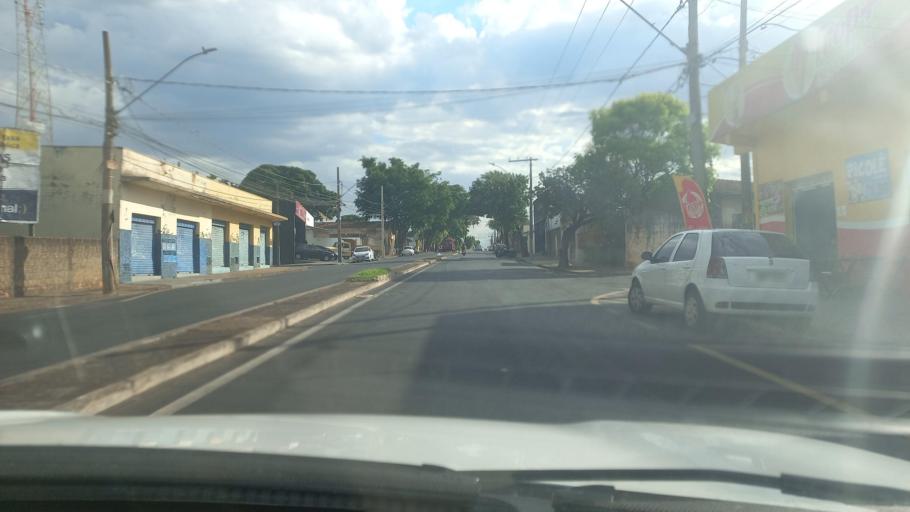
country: BR
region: Minas Gerais
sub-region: Uberaba
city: Uberaba
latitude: -19.7628
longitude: -47.9166
